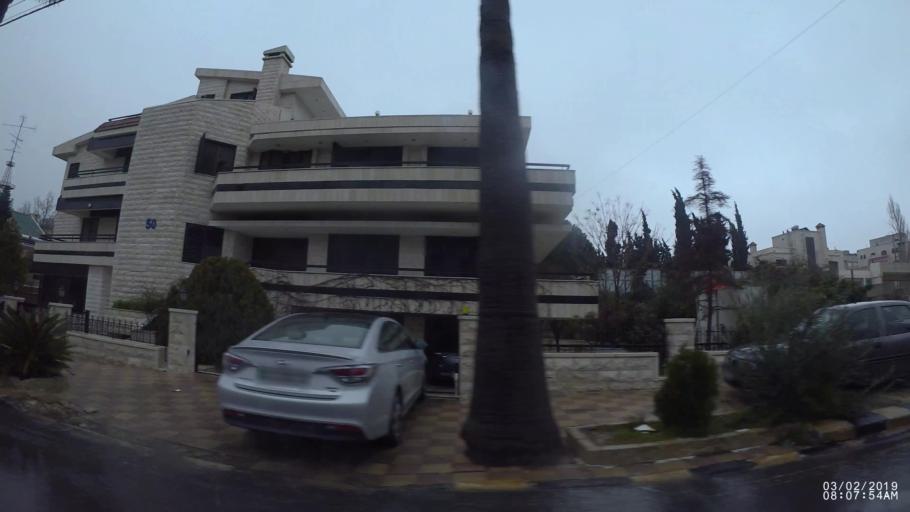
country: JO
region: Amman
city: Wadi as Sir
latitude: 31.9675
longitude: 35.8710
